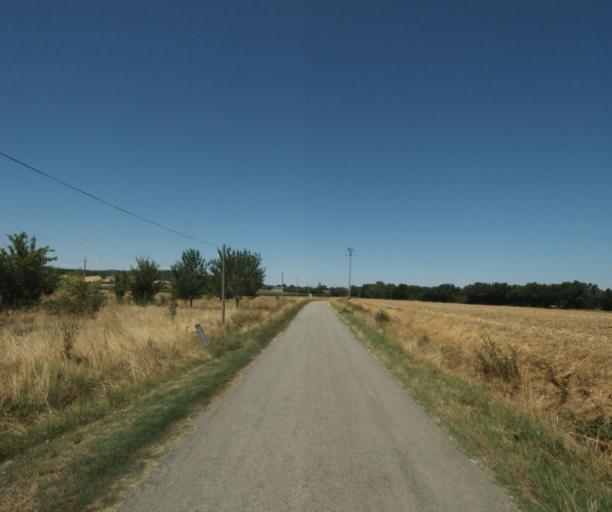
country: FR
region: Midi-Pyrenees
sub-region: Departement de la Haute-Garonne
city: Saint-Felix-Lauragais
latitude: 43.4512
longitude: 1.9372
